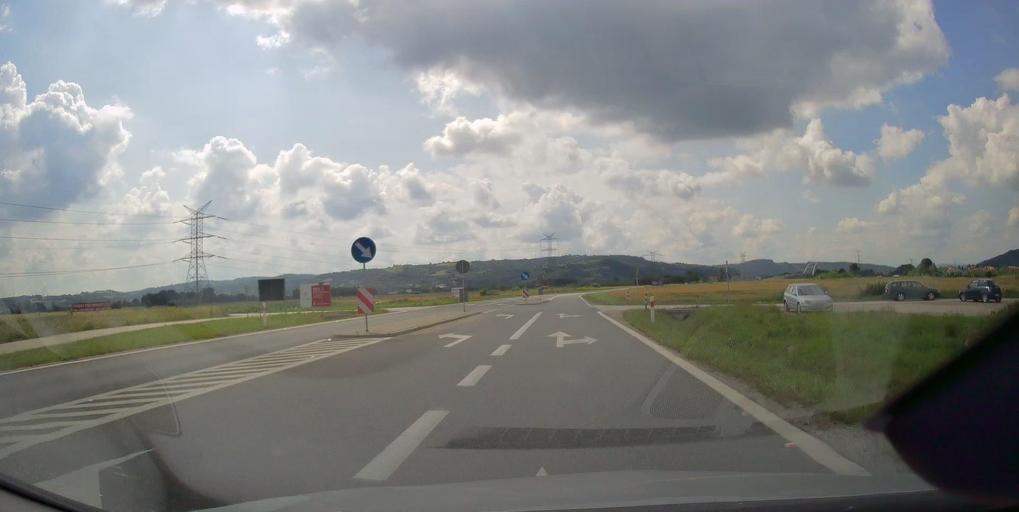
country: PL
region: Lesser Poland Voivodeship
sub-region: Powiat tarnowski
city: Wojnicz
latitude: 49.9596
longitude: 20.8514
